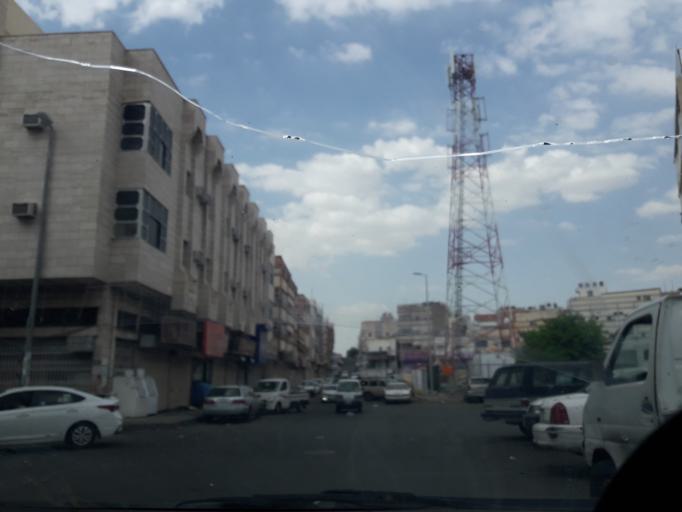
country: SA
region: Makkah
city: Ta'if
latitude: 21.2601
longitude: 40.4236
